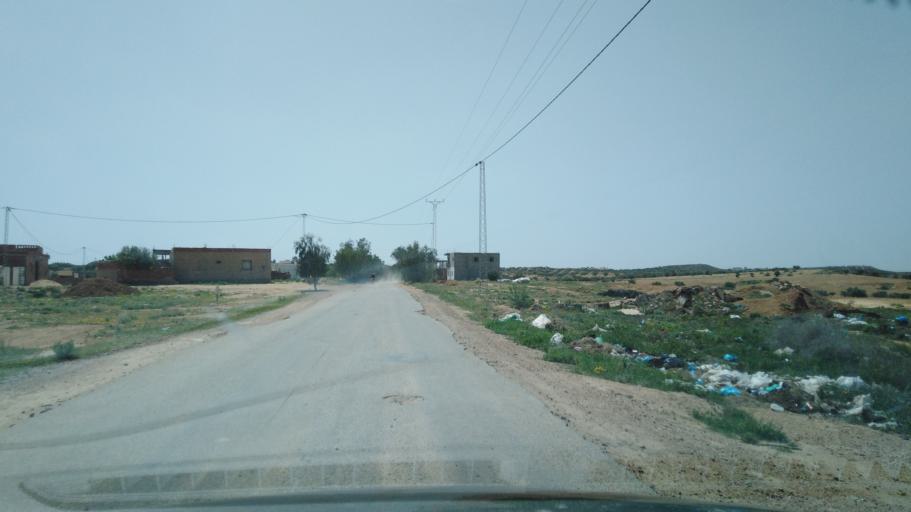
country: TN
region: Safaqis
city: Sfax
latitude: 34.7256
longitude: 10.5294
